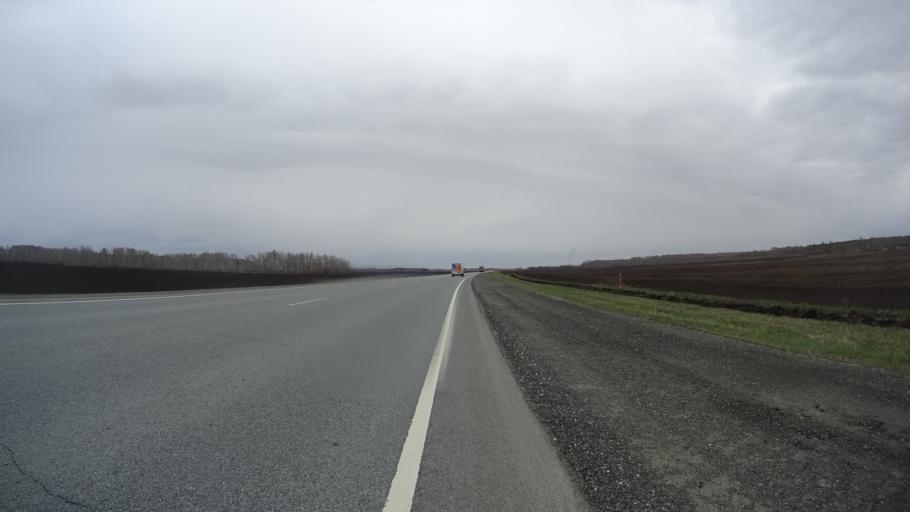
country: RU
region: Chelyabinsk
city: Krasnogorskiy
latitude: 54.5779
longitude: 61.2915
